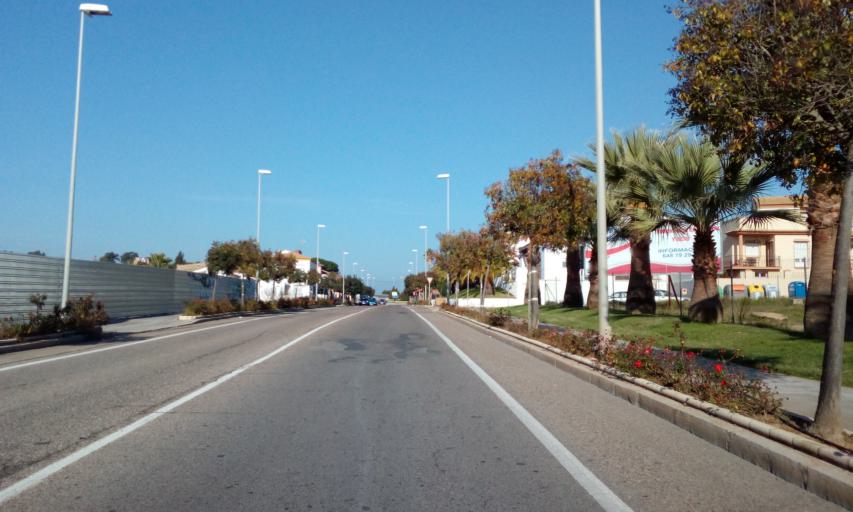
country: ES
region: Andalusia
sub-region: Provincia de Huelva
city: Ayamonte
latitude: 37.2240
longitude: -7.4020
